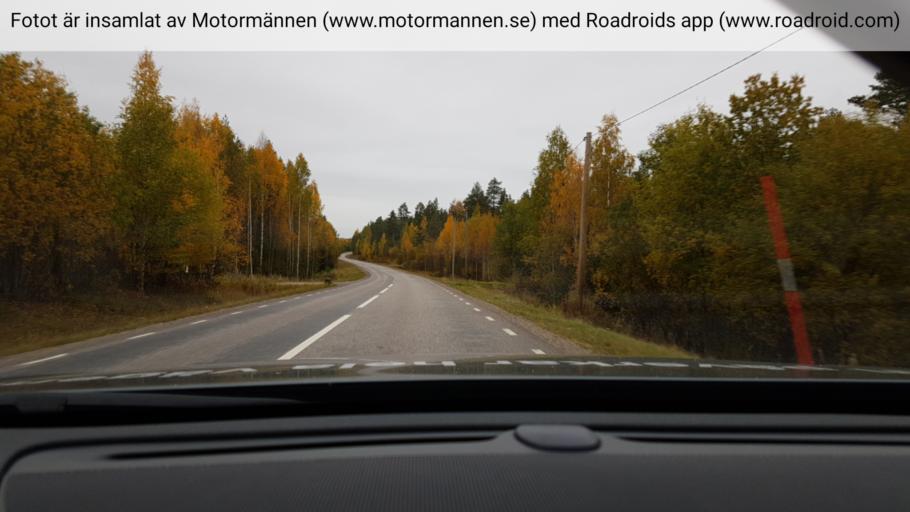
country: SE
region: Norrbotten
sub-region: Overkalix Kommun
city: OEverkalix
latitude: 66.5322
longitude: 22.7571
